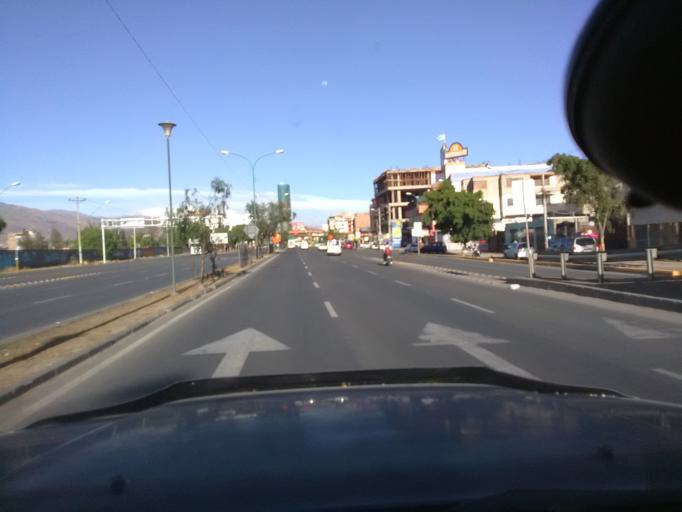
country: BO
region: Cochabamba
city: Cochabamba
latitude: -17.3934
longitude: -66.1832
